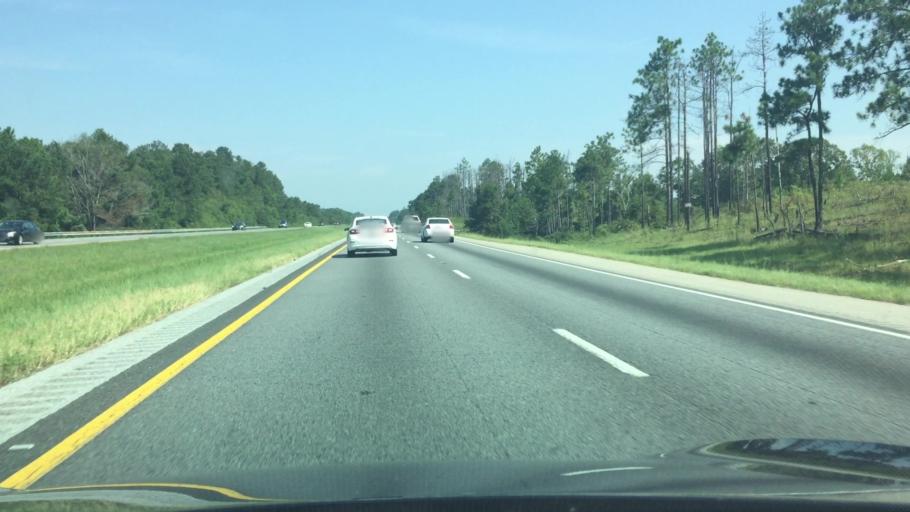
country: US
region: Alabama
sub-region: Autauga County
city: Marbury
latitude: 32.6809
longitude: -86.5121
